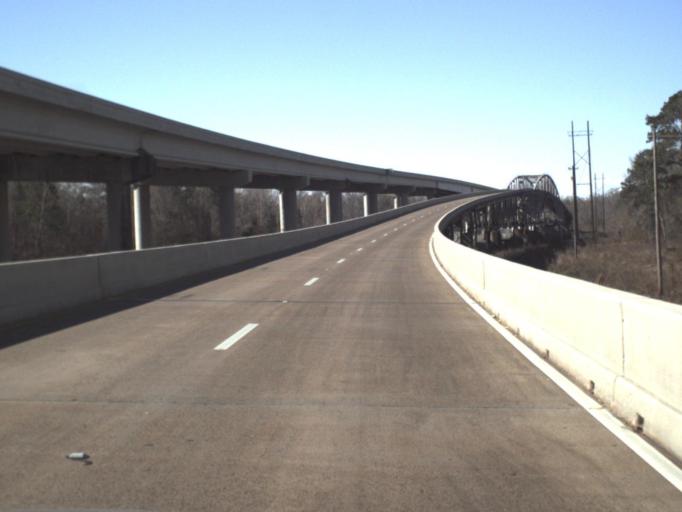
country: US
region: Florida
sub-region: Liberty County
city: Bristol
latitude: 30.4343
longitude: -84.9988
